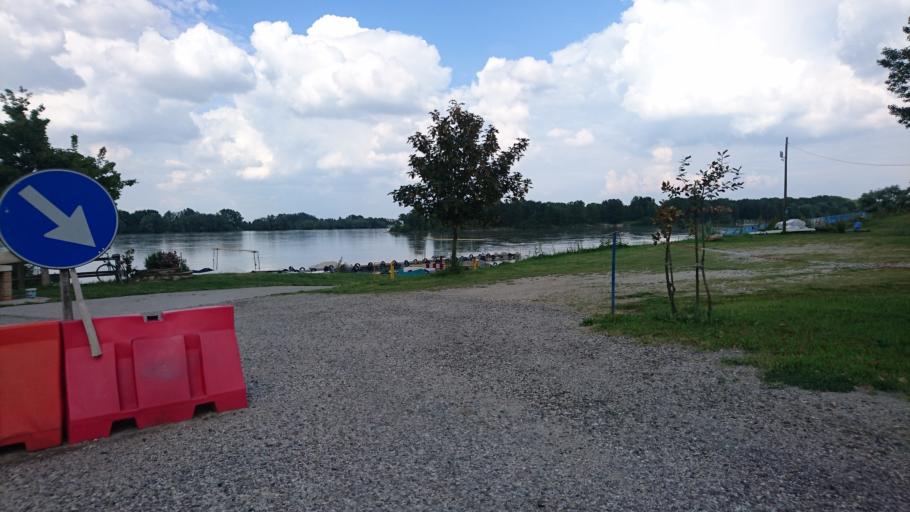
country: IT
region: Lombardy
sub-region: Provincia di Mantova
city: Sermide
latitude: 45.0125
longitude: 11.2937
